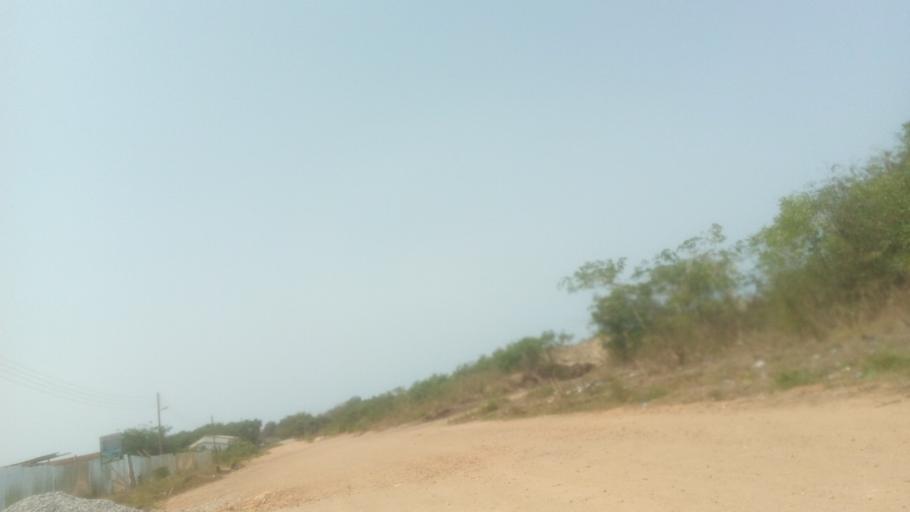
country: GH
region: Central
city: Winneba
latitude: 5.3693
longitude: -0.6330
